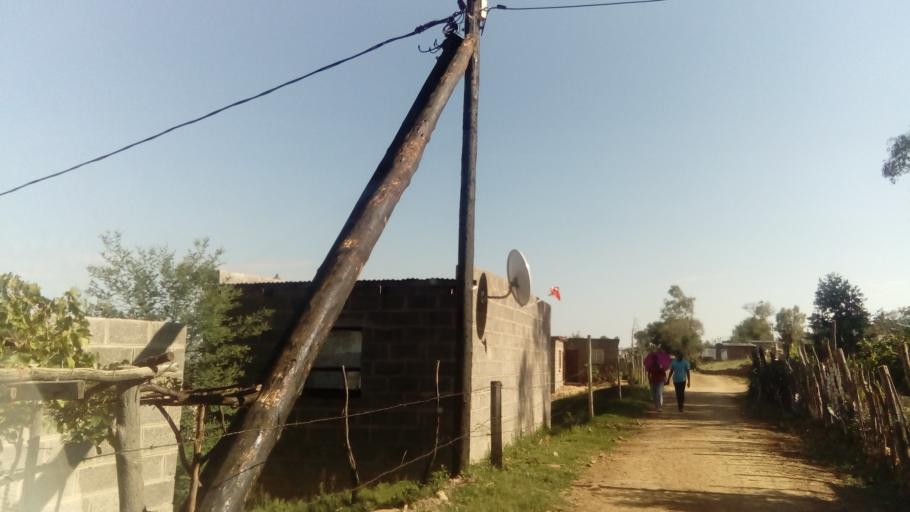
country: LS
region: Berea
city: Teyateyaneng
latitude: -29.1436
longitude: 27.7479
